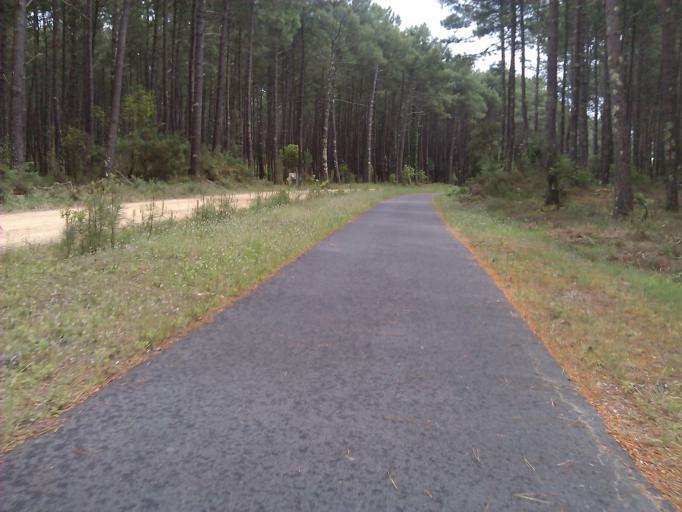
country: FR
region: Aquitaine
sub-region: Departement des Landes
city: Vielle-Saint-Girons
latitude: 43.9338
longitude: -1.3534
